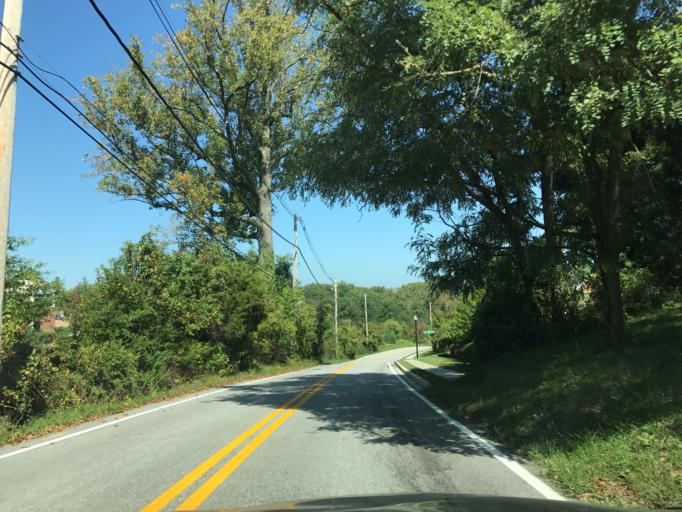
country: US
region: Maryland
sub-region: Howard County
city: Ellicott City
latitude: 39.2412
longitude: -76.8006
